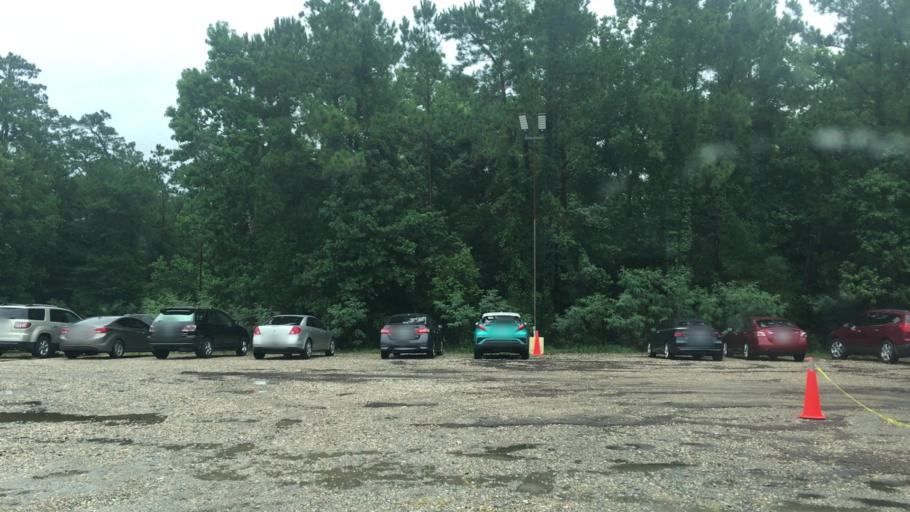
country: US
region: Texas
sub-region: Harris County
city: Atascocita
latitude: 29.9856
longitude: -95.2029
